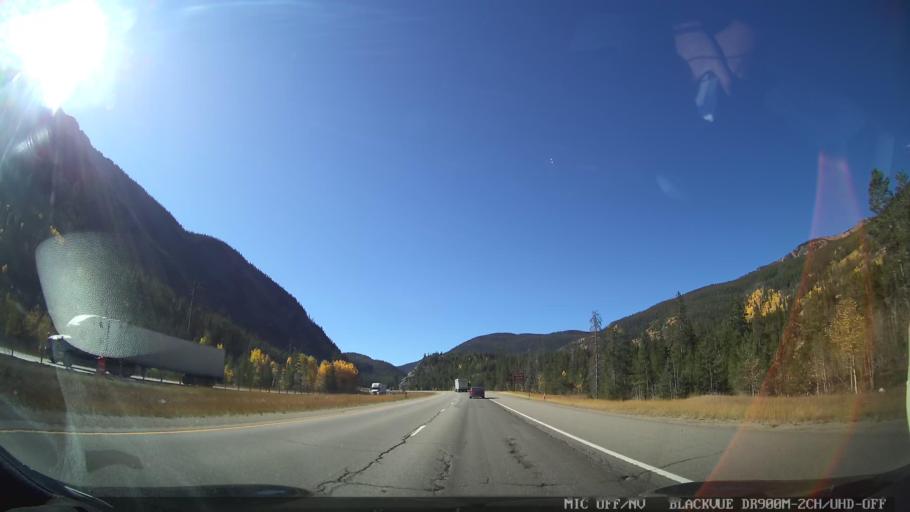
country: US
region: Colorado
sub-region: Summit County
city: Frisco
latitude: 39.5486
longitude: -106.1381
